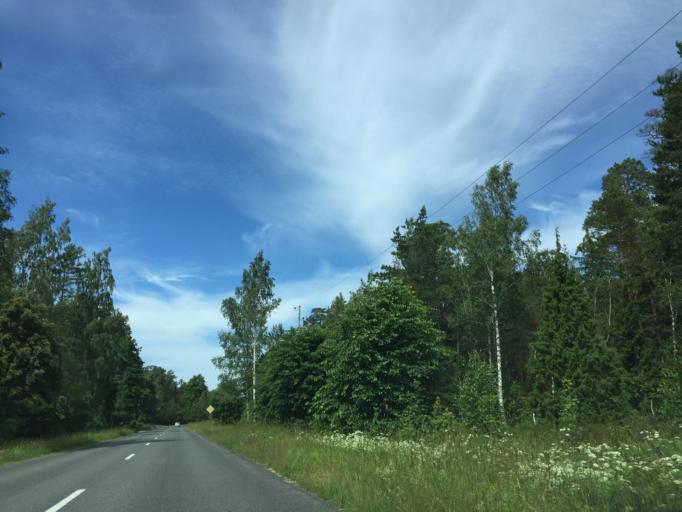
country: LV
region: Dundaga
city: Dundaga
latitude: 57.6580
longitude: 22.5714
